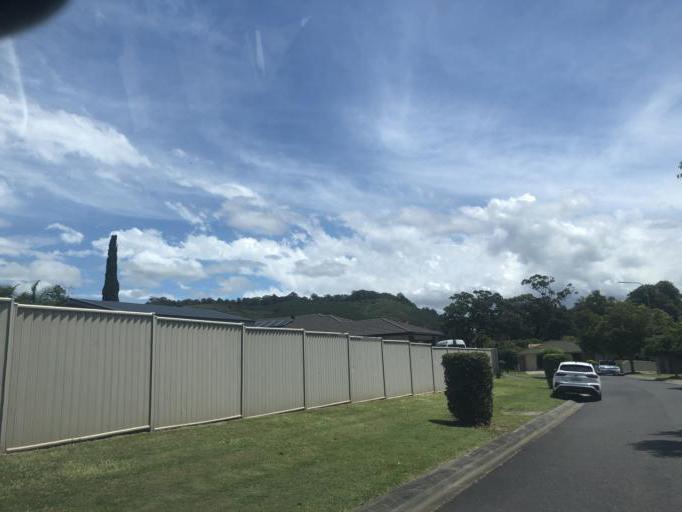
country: AU
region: New South Wales
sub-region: Coffs Harbour
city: Coffs Harbour
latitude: -30.2897
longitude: 153.0922
